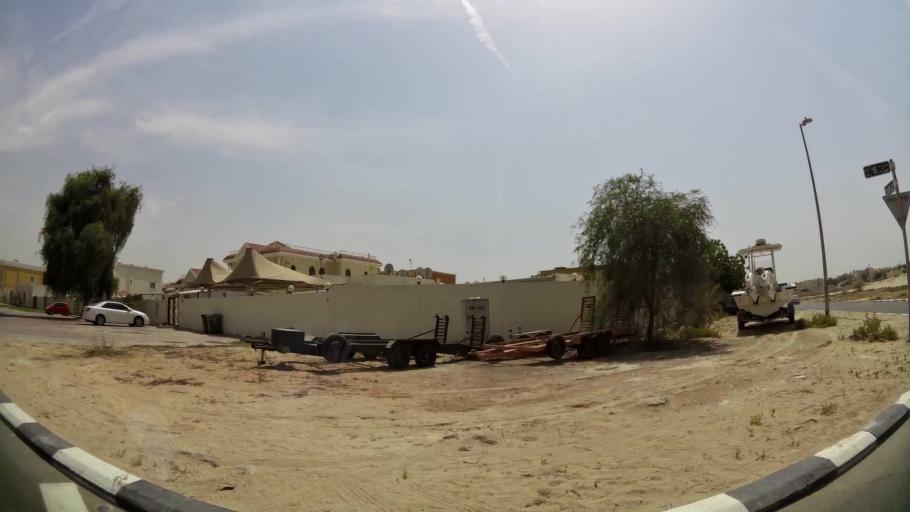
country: AE
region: Ash Shariqah
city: Sharjah
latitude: 25.2400
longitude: 55.4369
